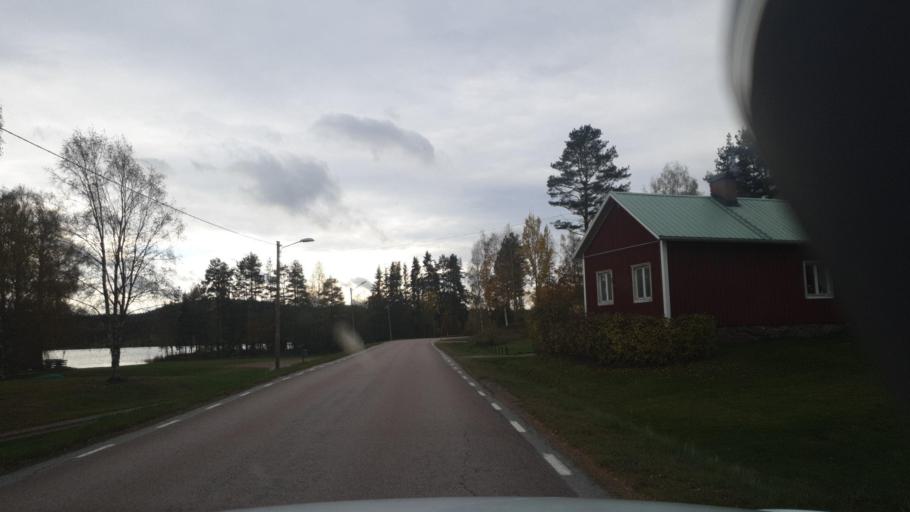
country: SE
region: Vaermland
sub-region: Arvika Kommun
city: Arvika
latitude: 59.7380
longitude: 12.8101
